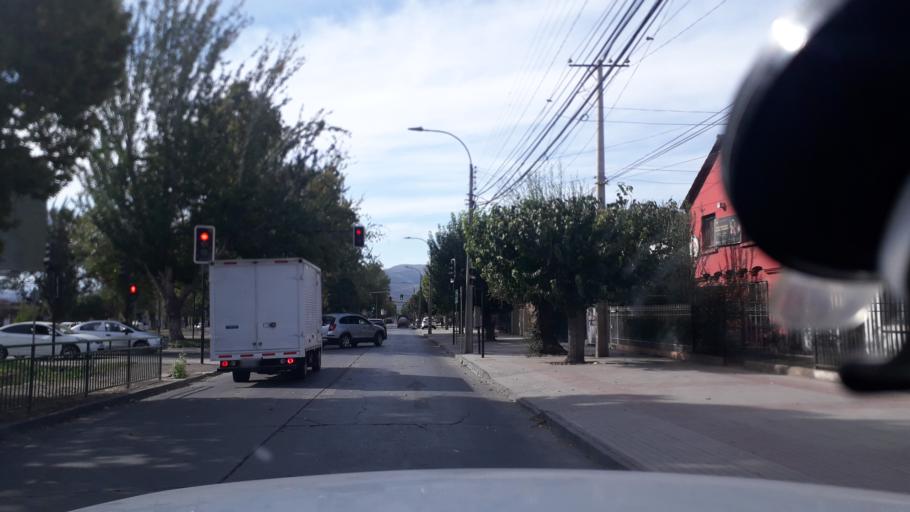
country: CL
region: Valparaiso
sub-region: Provincia de San Felipe
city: San Felipe
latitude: -32.7528
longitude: -70.7204
